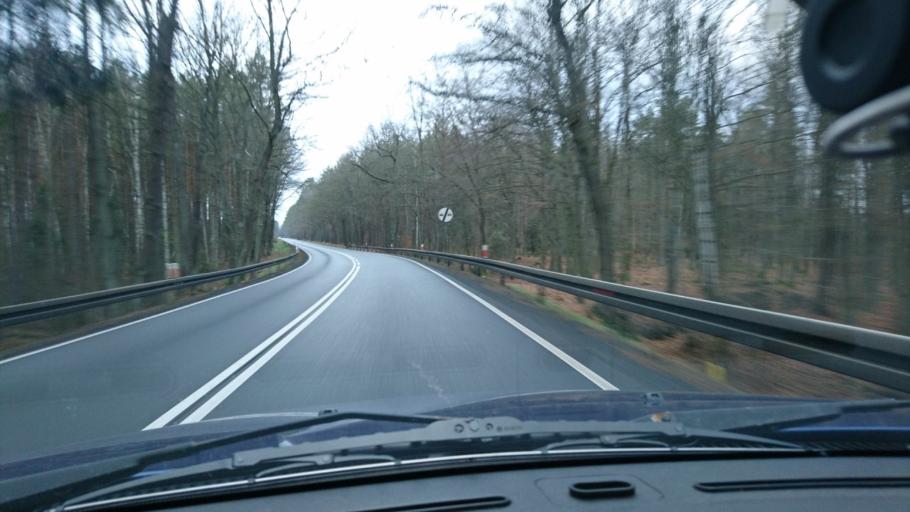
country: PL
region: Opole Voivodeship
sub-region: Powiat oleski
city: Olesno
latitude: 50.9365
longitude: 18.3303
